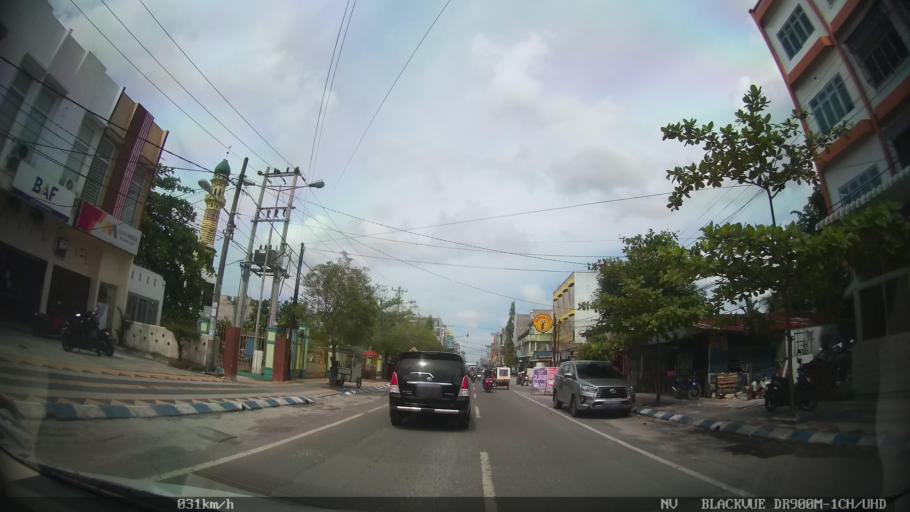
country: ID
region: North Sumatra
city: Percut
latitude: 3.5602
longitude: 98.8726
